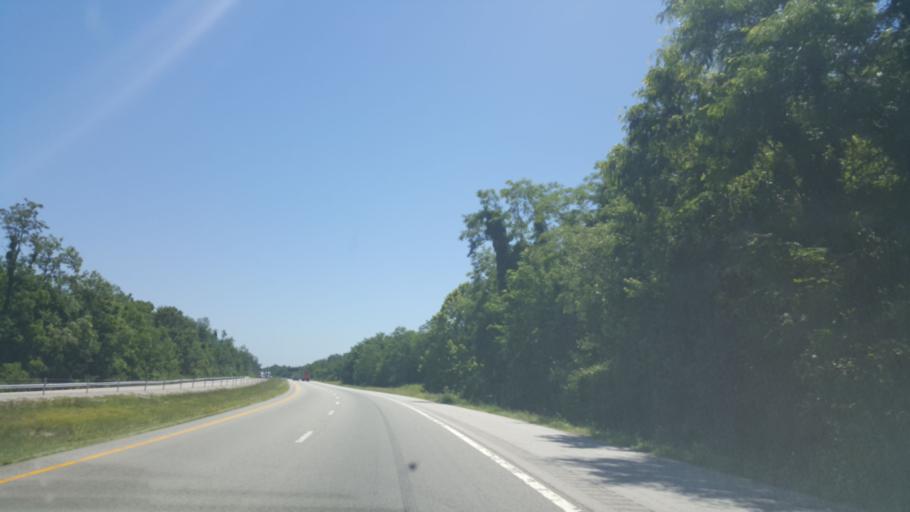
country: US
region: Tennessee
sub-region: Roane County
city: Rockwood
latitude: 35.8830
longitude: -84.8150
